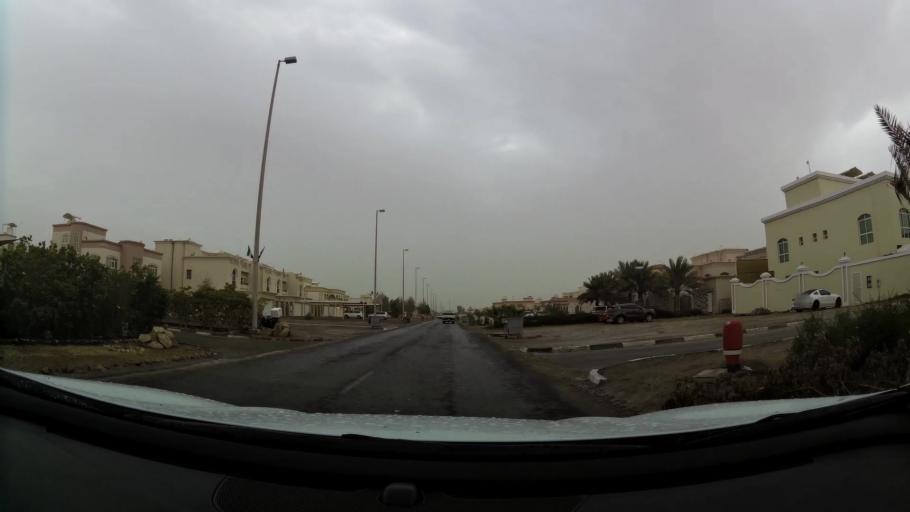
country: AE
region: Abu Dhabi
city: Abu Dhabi
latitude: 24.4152
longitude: 54.5854
